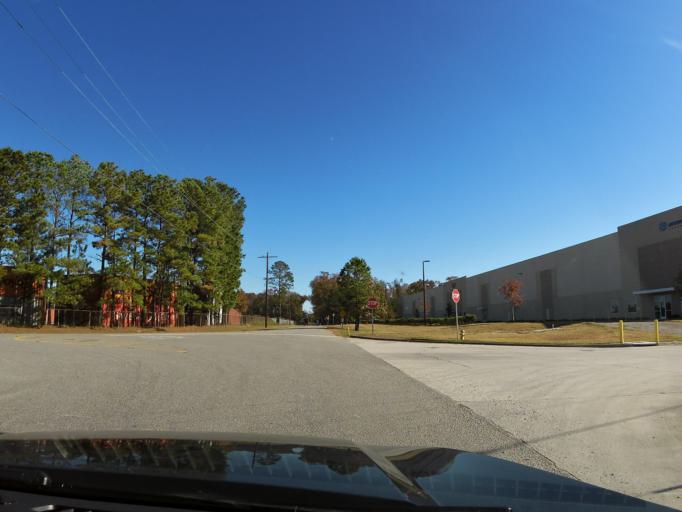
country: US
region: Georgia
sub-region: Chatham County
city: Savannah
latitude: 32.0648
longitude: -81.1444
